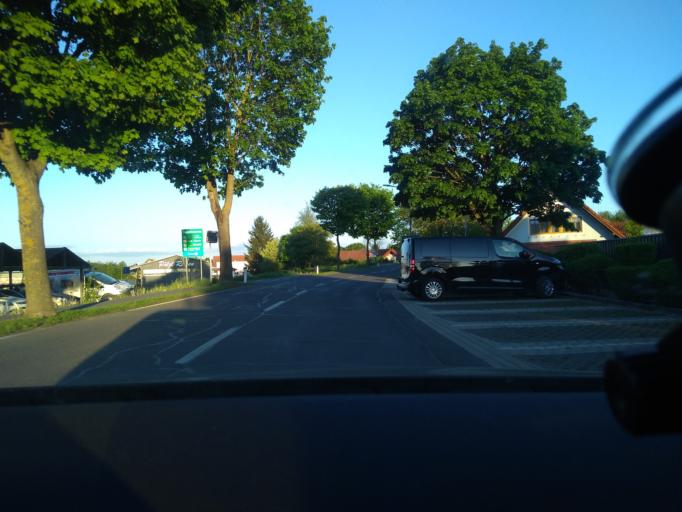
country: AT
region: Styria
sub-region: Politischer Bezirk Voitsberg
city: Mooskirchen
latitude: 46.9832
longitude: 15.2843
